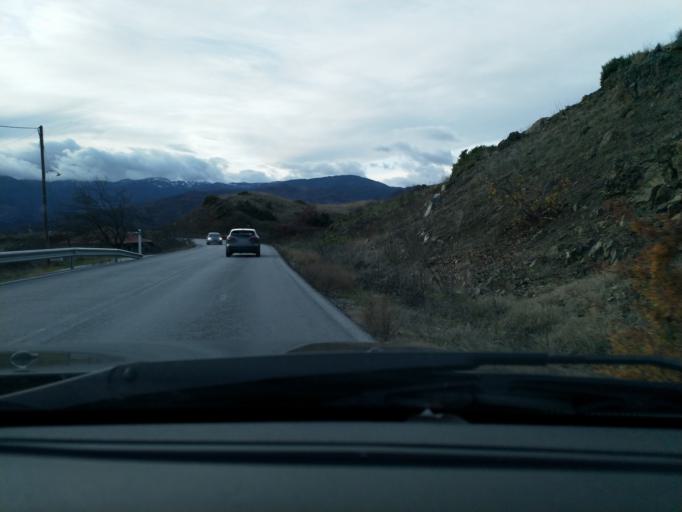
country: GR
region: Epirus
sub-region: Nomos Ioanninon
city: Metsovo
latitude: 39.7862
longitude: 21.3835
